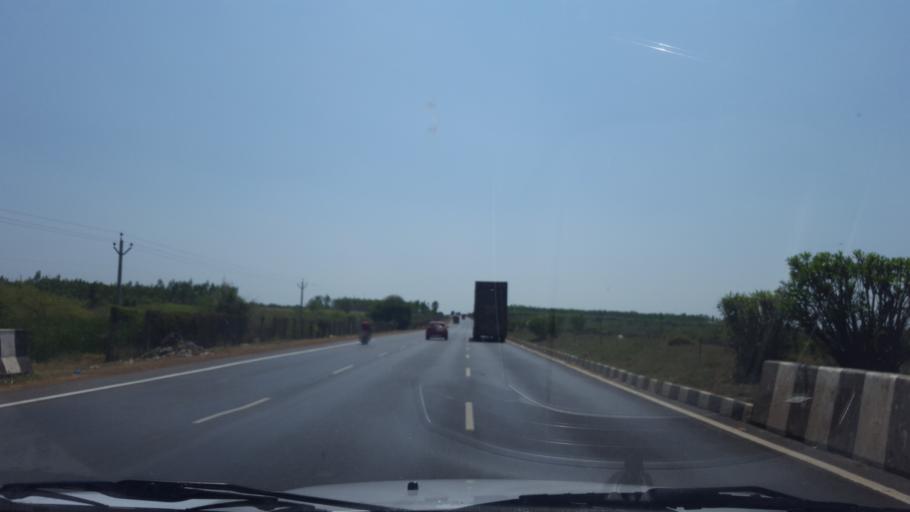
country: IN
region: Andhra Pradesh
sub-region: Nellore
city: Kavali
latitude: 14.7480
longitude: 79.9989
